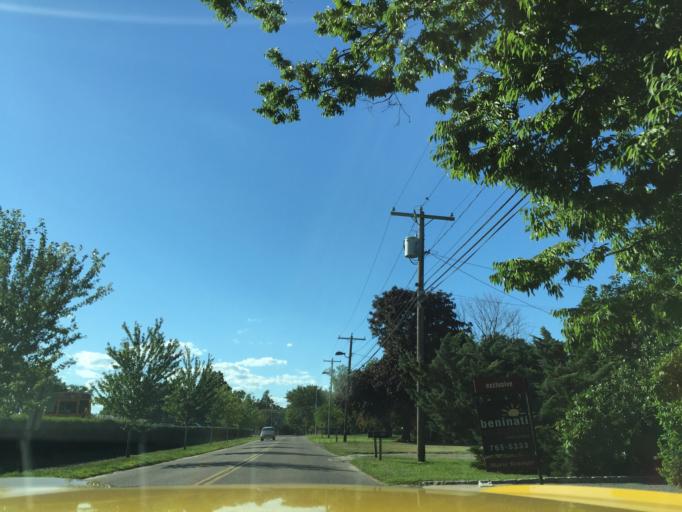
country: US
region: New York
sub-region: Suffolk County
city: Southold
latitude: 41.0593
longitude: -72.4298
